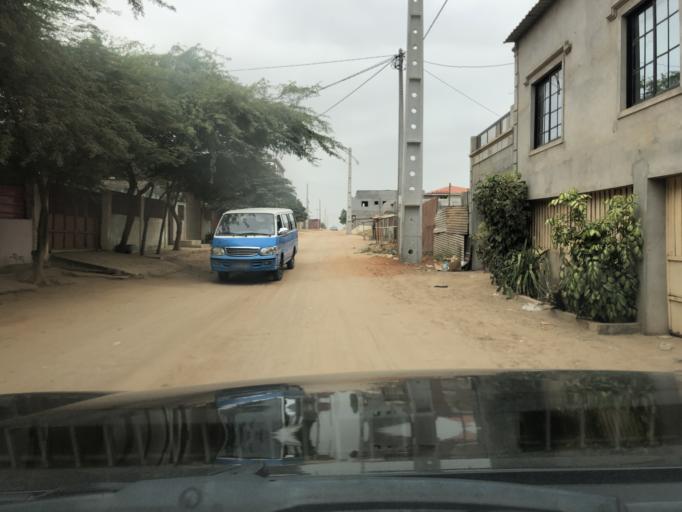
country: AO
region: Luanda
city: Luanda
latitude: -8.9376
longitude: 13.2274
